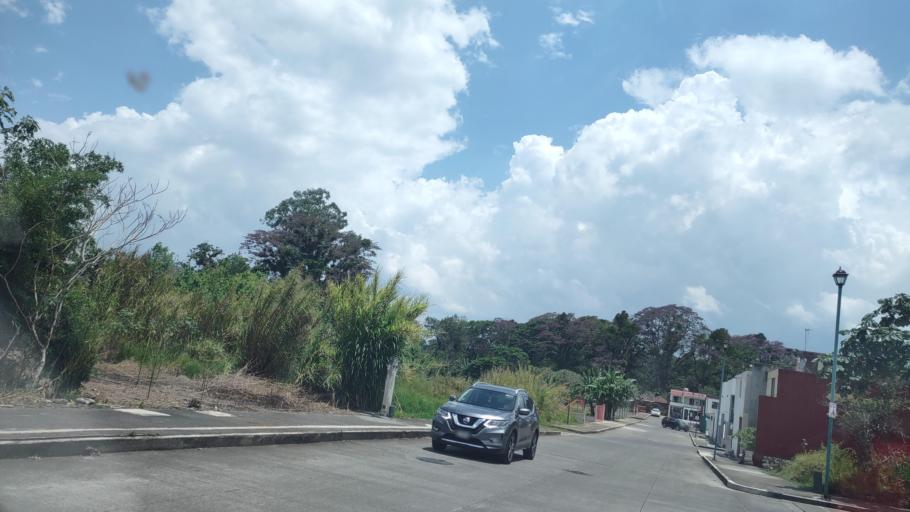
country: MX
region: Veracruz
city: Coatepec
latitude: 19.4469
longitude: -96.9491
